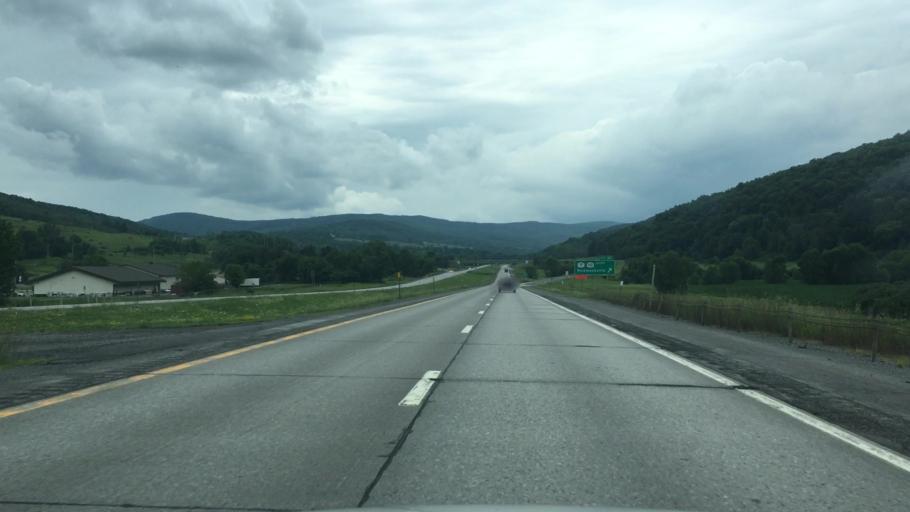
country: US
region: New York
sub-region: Schoharie County
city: Cobleskill
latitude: 42.6448
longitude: -74.5366
